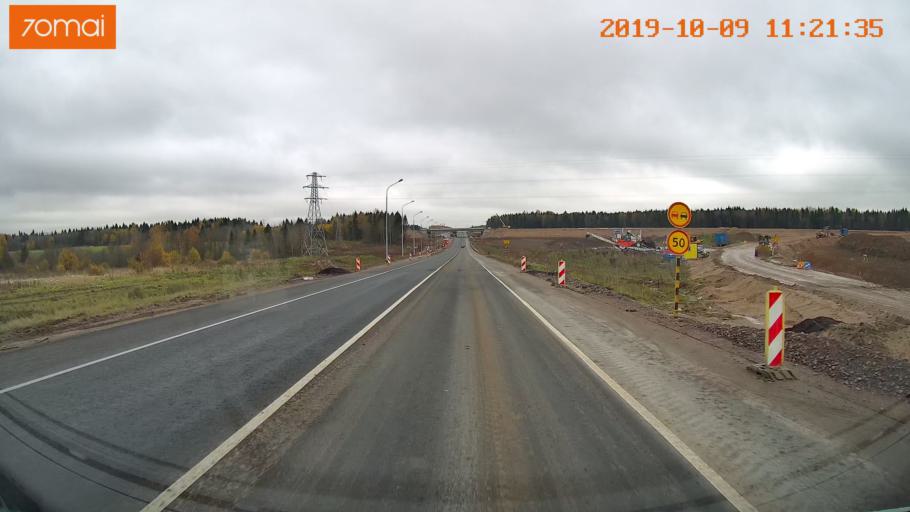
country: RU
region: Vologda
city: Vologda
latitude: 59.1384
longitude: 39.9506
